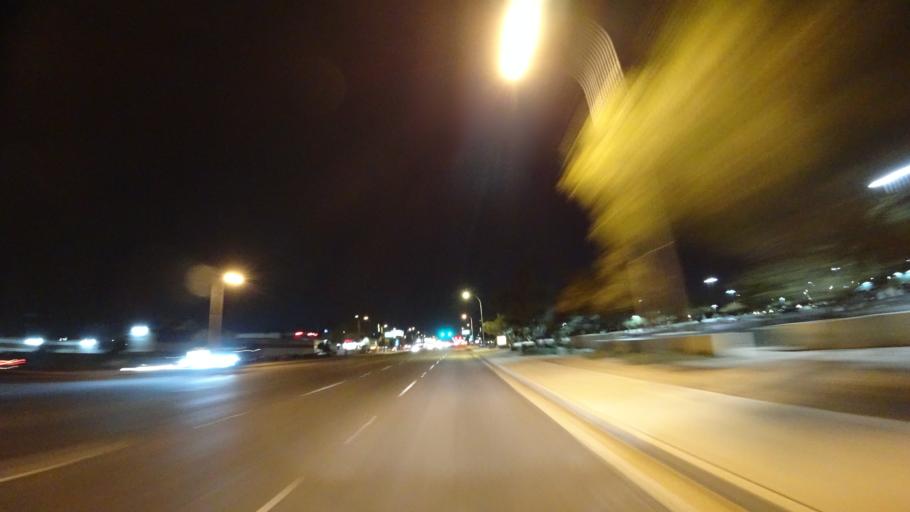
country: US
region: Arizona
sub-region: Maricopa County
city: Guadalupe
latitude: 33.3784
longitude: -111.9596
